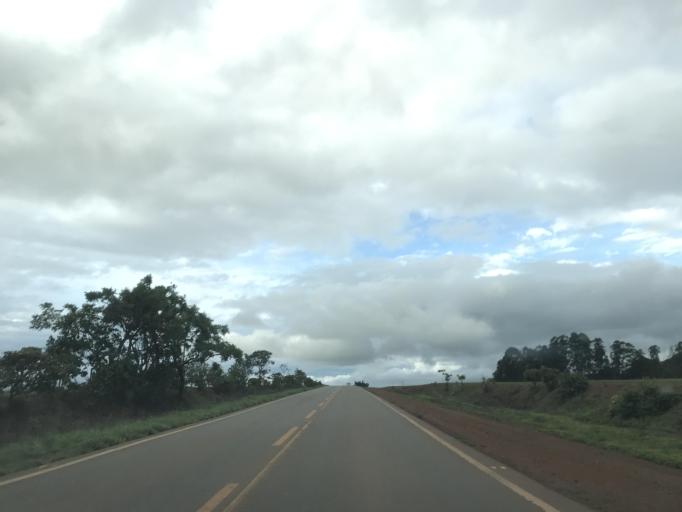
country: BR
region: Goias
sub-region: Luziania
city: Luziania
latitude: -16.4554
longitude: -48.2078
